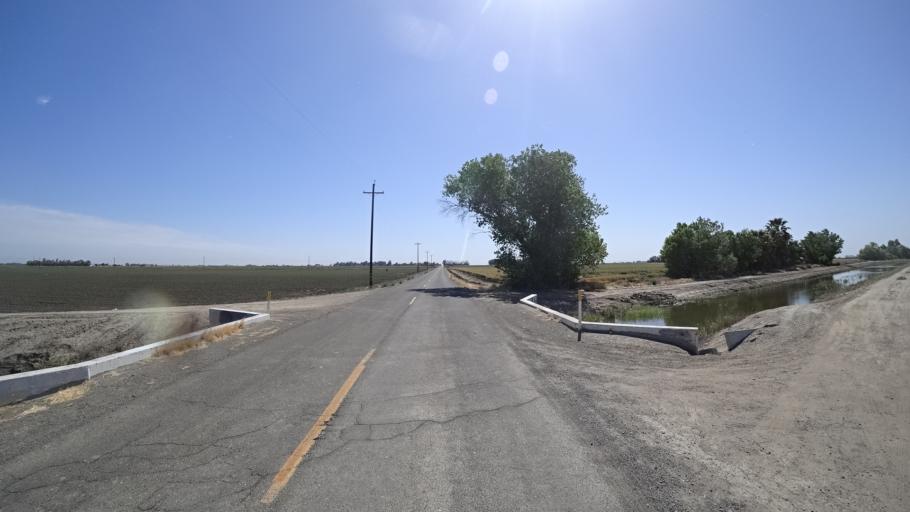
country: US
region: California
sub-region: Kings County
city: Stratford
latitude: 36.1968
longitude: -119.8194
